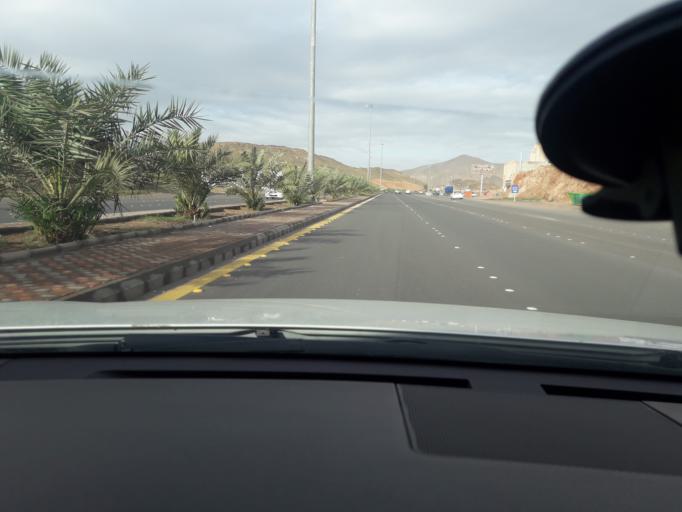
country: SA
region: Al Madinah al Munawwarah
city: Sultanah
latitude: 24.4658
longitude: 39.5069
